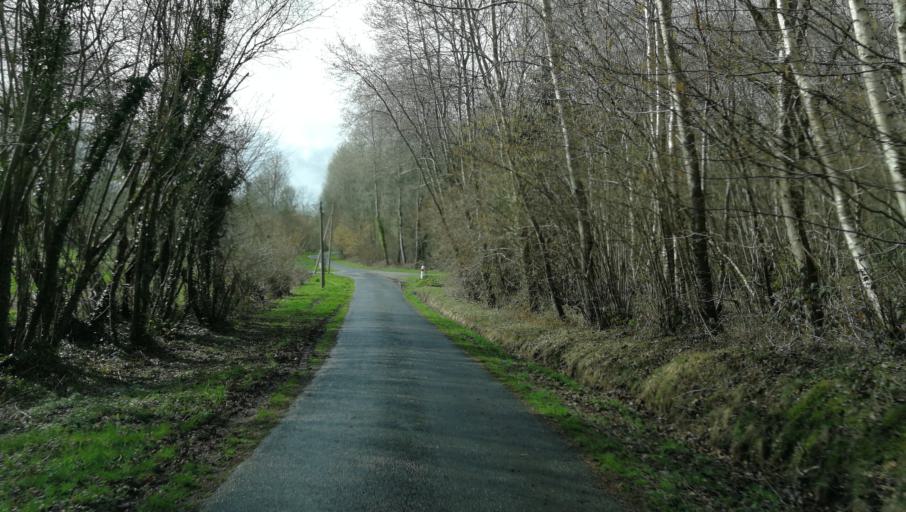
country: FR
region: Haute-Normandie
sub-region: Departement de l'Eure
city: Lieurey
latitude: 49.2343
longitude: 0.5509
